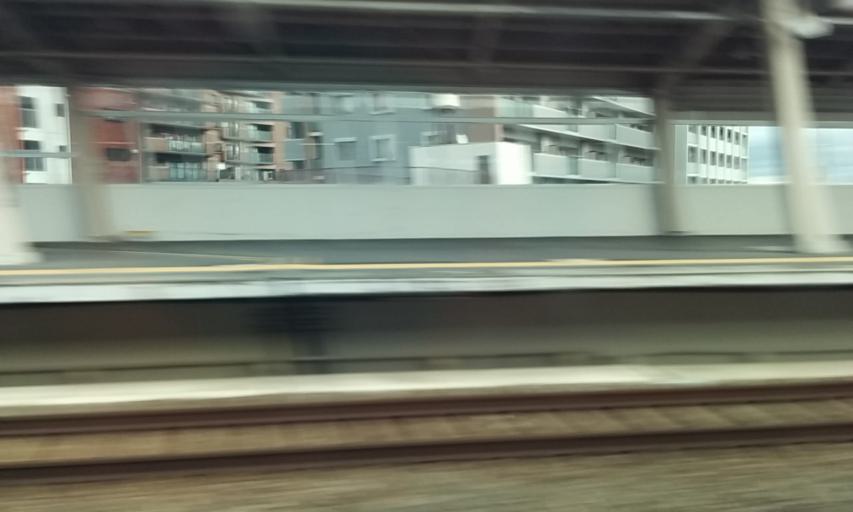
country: JP
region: Hyogo
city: Akashi
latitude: 34.6670
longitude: 134.9591
